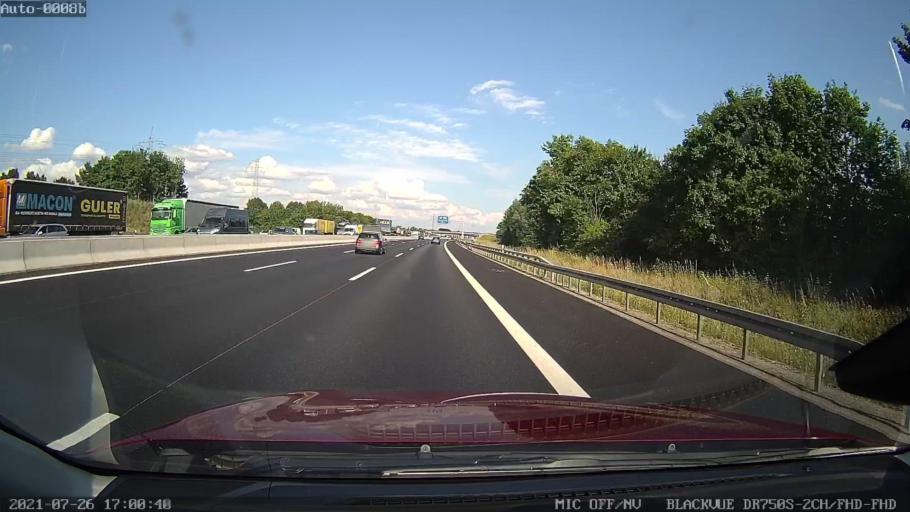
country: DE
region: Bavaria
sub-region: Upper Palatinate
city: Tegernheim
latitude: 49.0005
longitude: 12.1720
